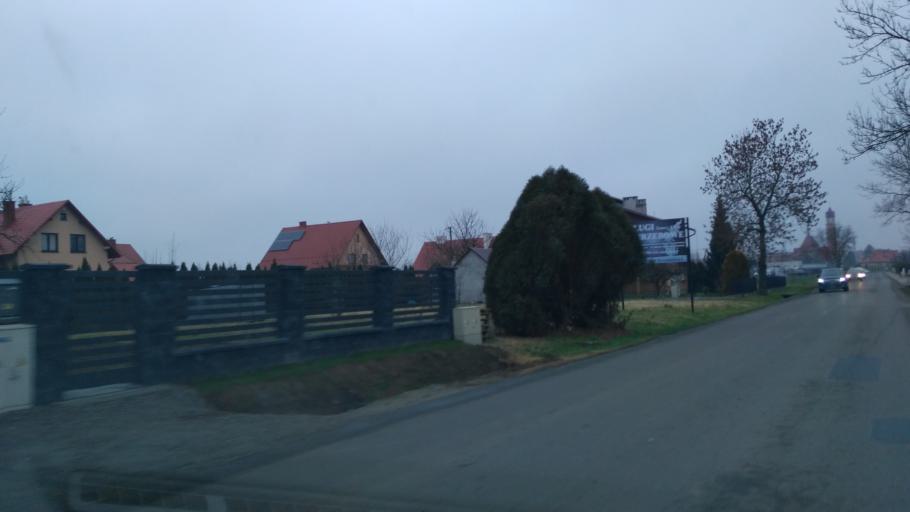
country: PL
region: Subcarpathian Voivodeship
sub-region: Powiat przeworski
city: Przeworsk
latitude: 50.0603
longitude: 22.5165
